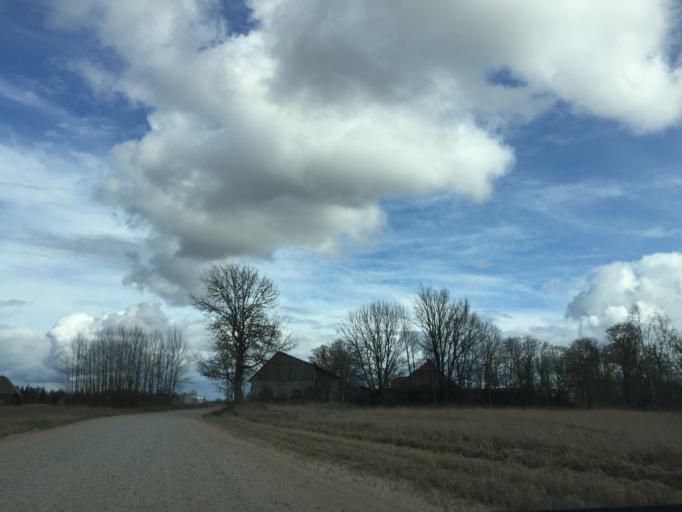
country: LV
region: Limbazu Rajons
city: Limbazi
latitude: 57.6080
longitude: 24.7916
